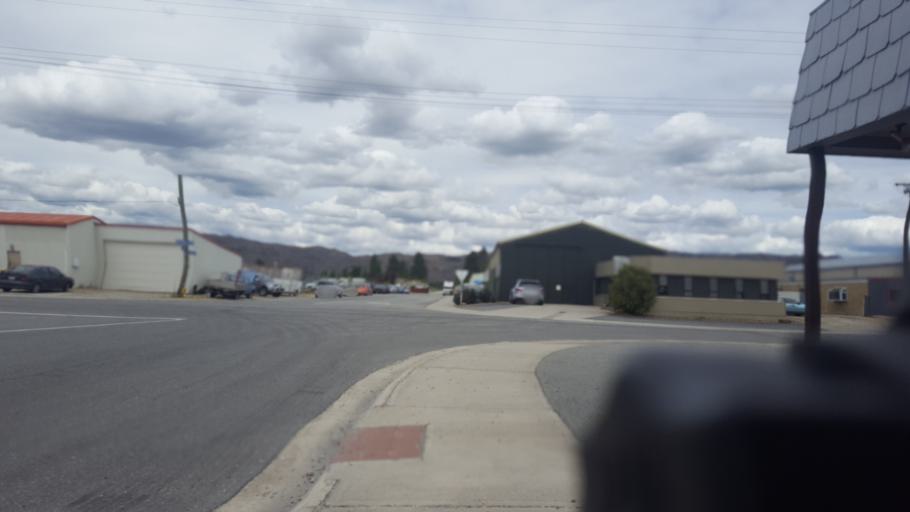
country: NZ
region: Otago
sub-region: Queenstown-Lakes District
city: Wanaka
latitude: -45.2476
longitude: 169.3727
